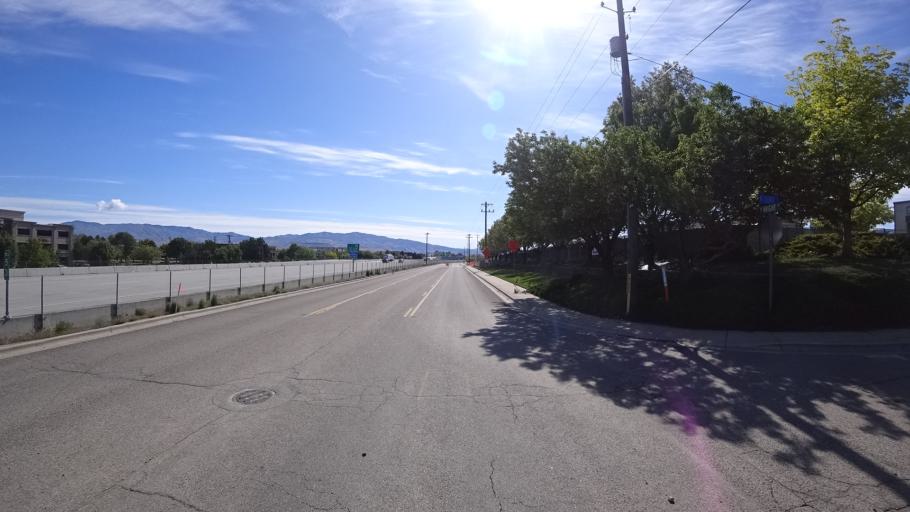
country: US
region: Idaho
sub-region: Ada County
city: Boise
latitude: 43.5716
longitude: -116.2252
